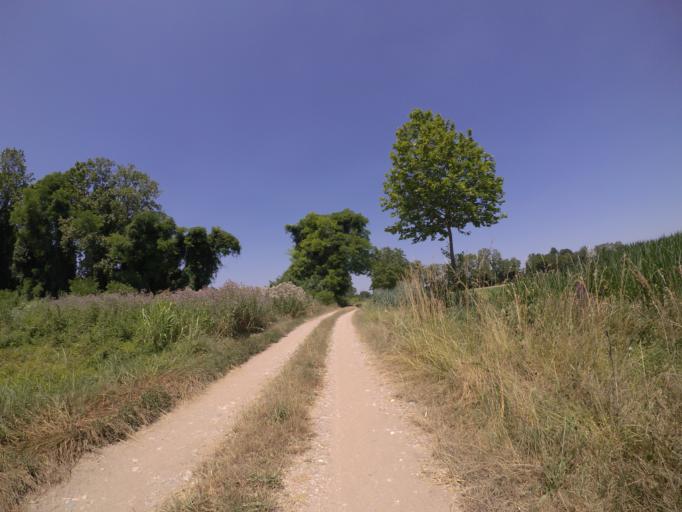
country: IT
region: Friuli Venezia Giulia
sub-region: Provincia di Udine
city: Talmassons
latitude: 45.9223
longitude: 13.0926
